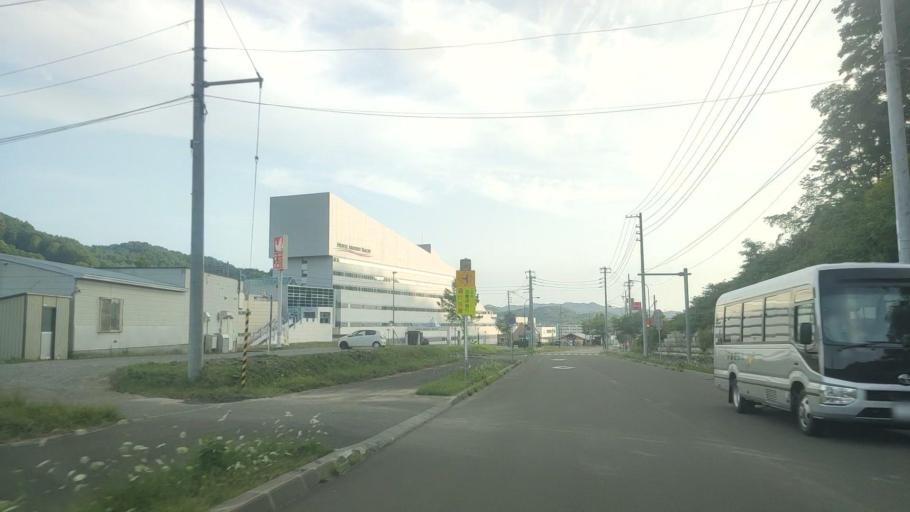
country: JP
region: Hokkaido
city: Iwamizawa
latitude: 43.0529
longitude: 141.9682
